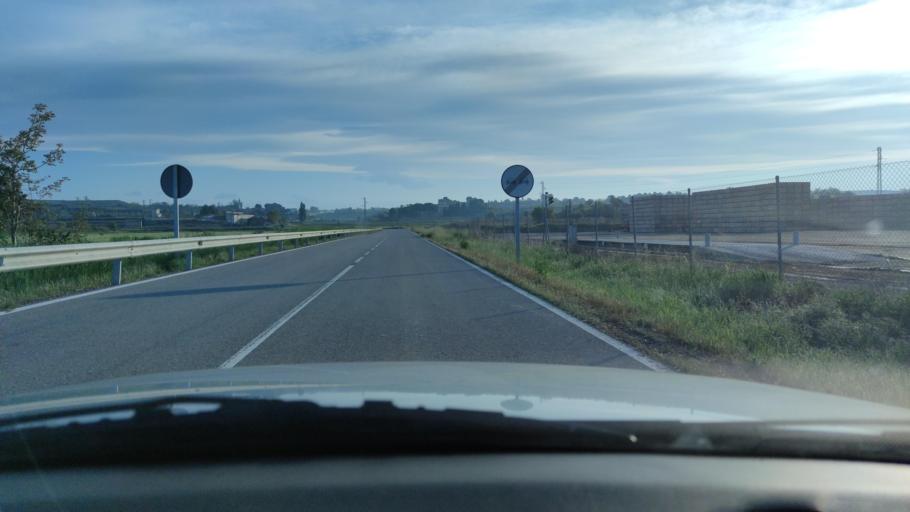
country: ES
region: Catalonia
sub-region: Provincia de Lleida
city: Castellsera
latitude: 41.7540
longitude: 0.9932
